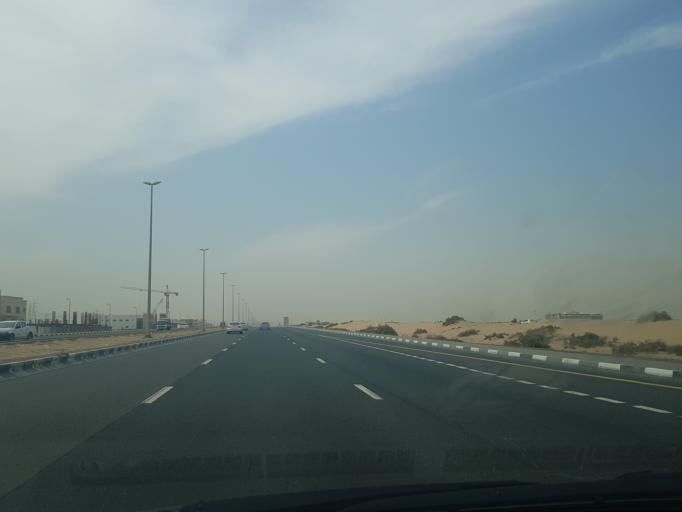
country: AE
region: Ash Shariqah
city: Sharjah
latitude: 25.2558
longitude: 55.5204
